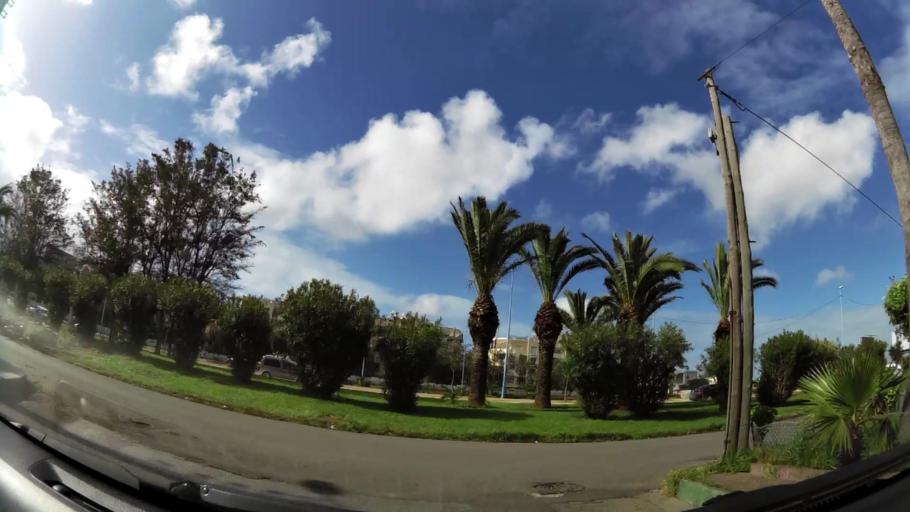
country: MA
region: Grand Casablanca
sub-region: Casablanca
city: Casablanca
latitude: 33.5528
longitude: -7.6241
